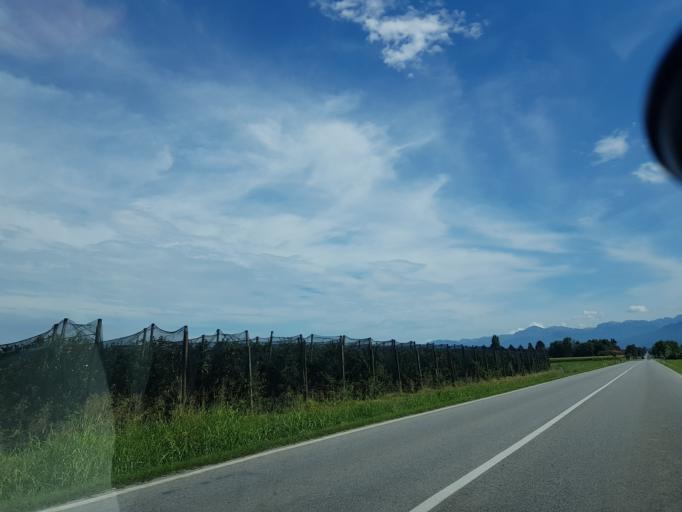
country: IT
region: Piedmont
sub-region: Provincia di Cuneo
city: Roata Rossi
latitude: 44.4677
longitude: 7.5138
